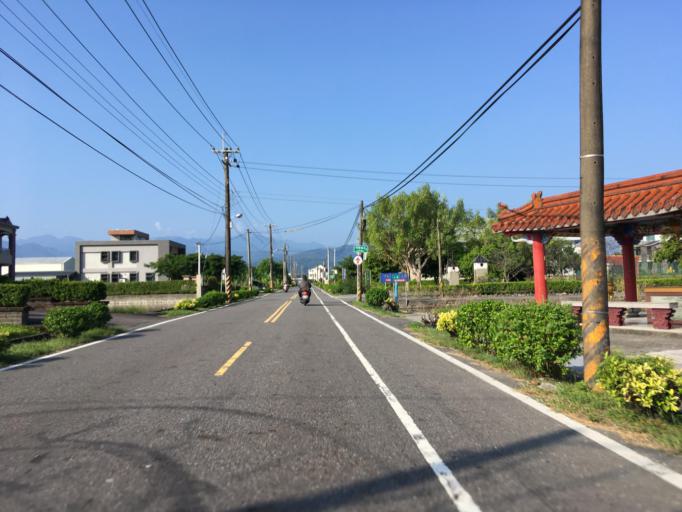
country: TW
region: Taiwan
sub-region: Yilan
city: Yilan
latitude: 24.6827
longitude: 121.7395
